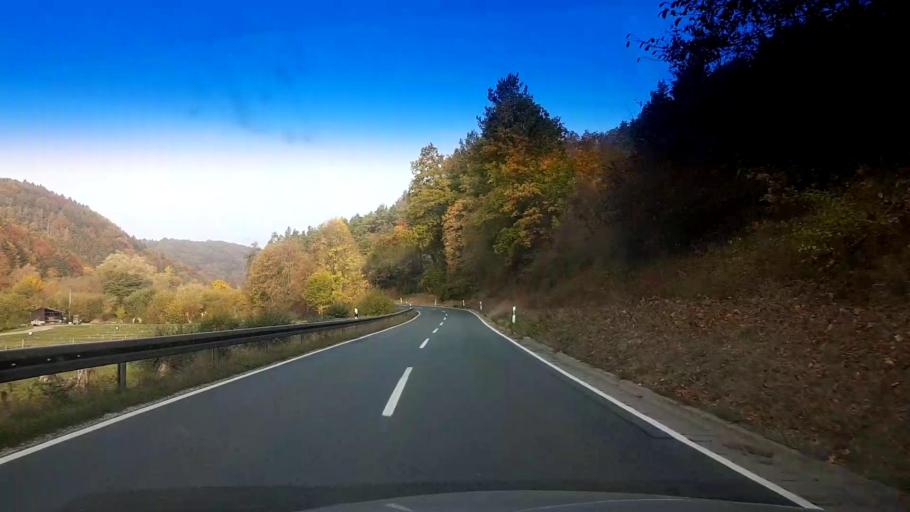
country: DE
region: Bavaria
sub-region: Upper Franconia
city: Weismain
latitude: 50.0530
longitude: 11.2284
